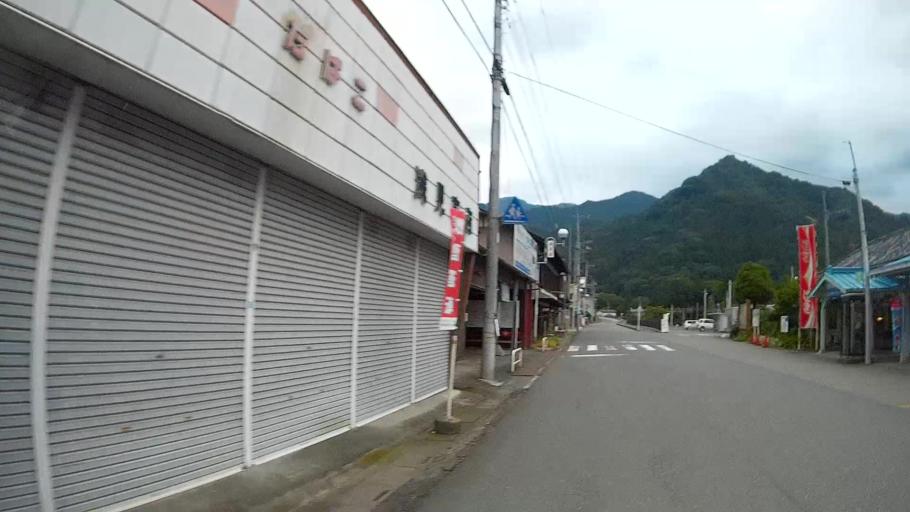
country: JP
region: Saitama
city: Chichibu
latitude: 35.9597
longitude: 138.9791
